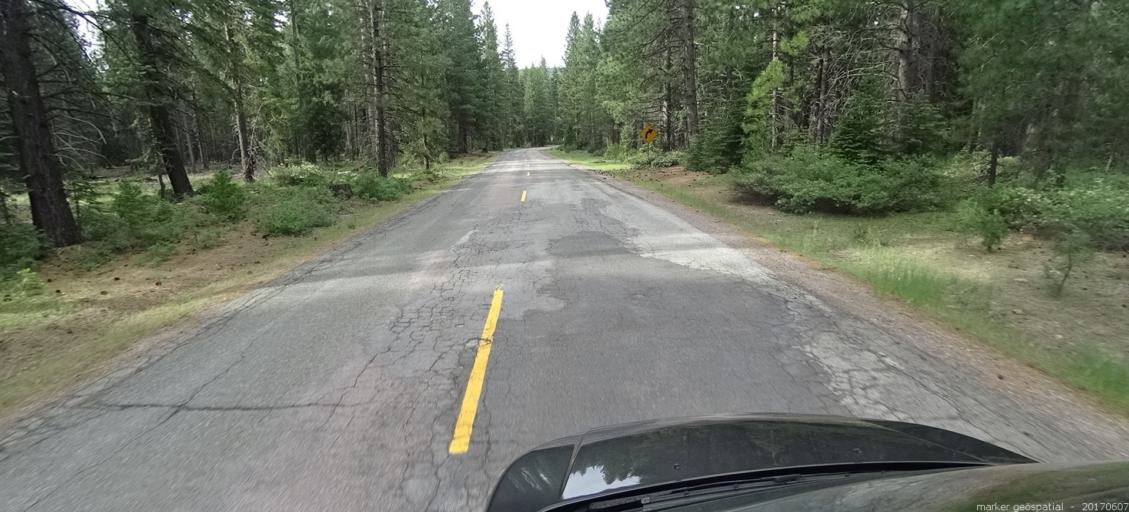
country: US
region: California
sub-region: Shasta County
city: Burney
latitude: 41.1846
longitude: -121.7074
